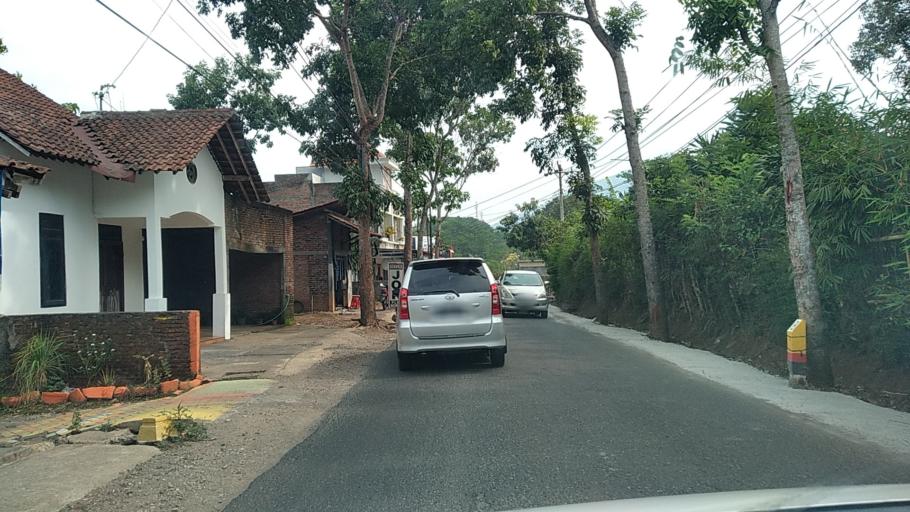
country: ID
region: Central Java
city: Ungaran
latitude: -7.0977
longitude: 110.3896
